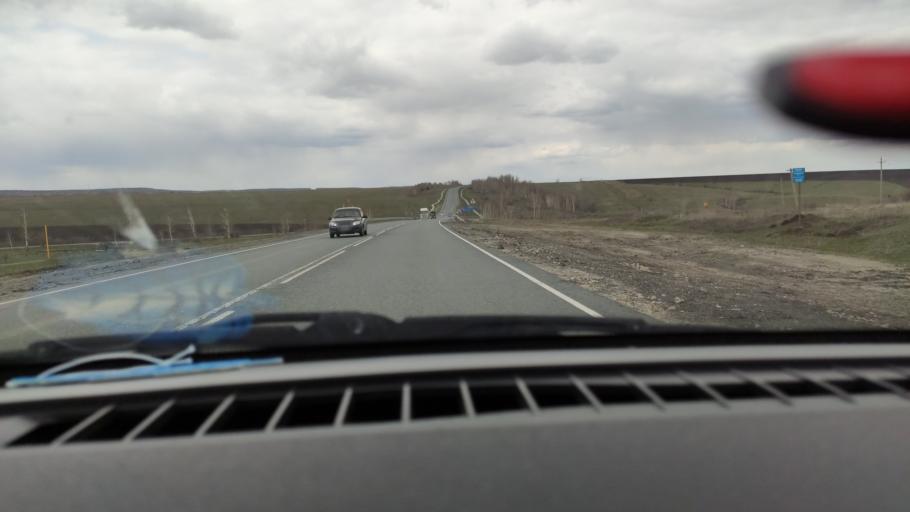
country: RU
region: Saratov
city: Shikhany
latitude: 52.1190
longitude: 47.2711
